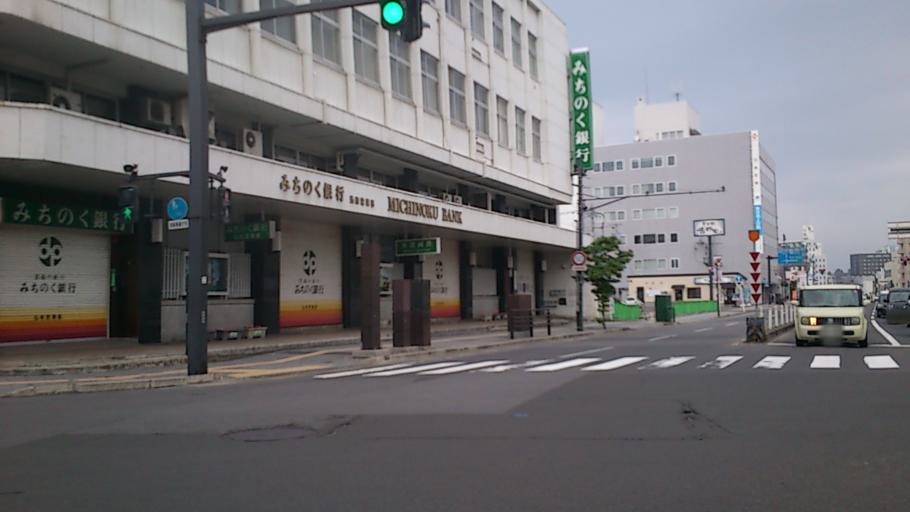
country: JP
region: Aomori
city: Hirosaki
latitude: 40.6005
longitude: 140.4786
